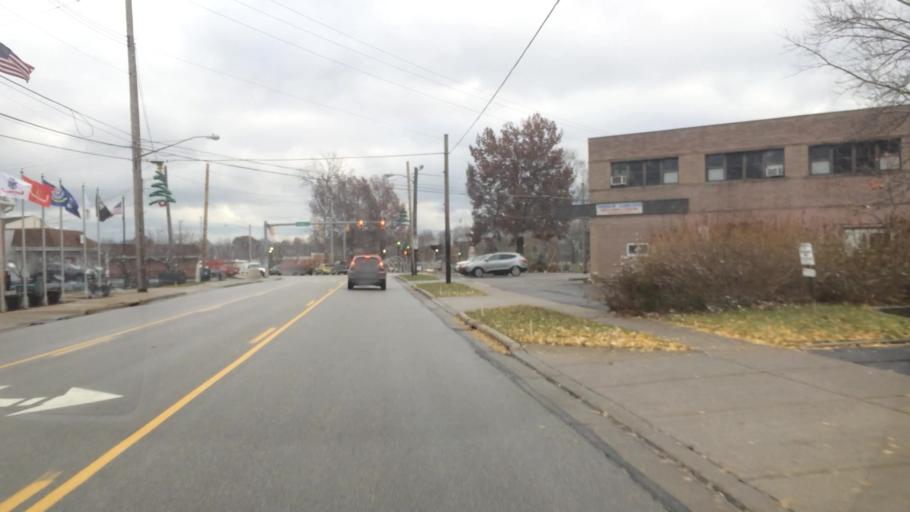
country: US
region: Ohio
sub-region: Summit County
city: Twinsburg
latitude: 41.3135
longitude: -81.4423
